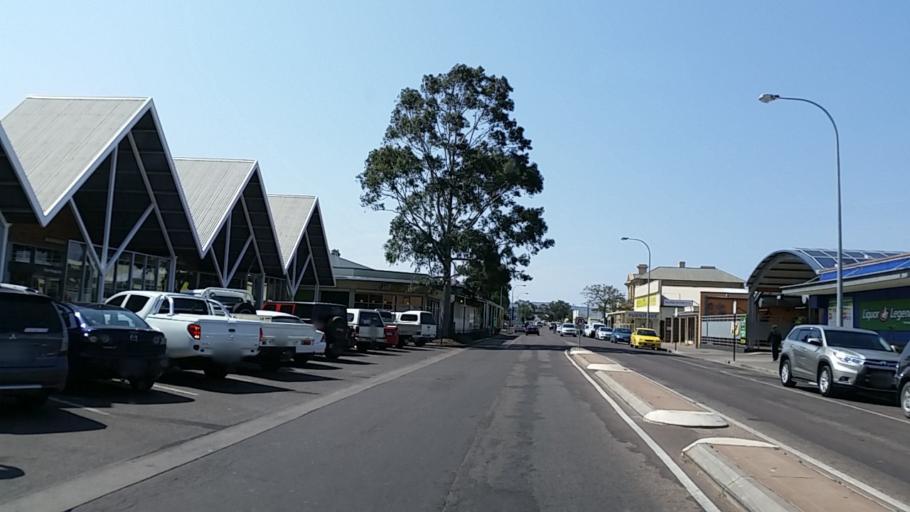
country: AU
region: South Australia
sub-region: Port Augusta
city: Port Augusta West
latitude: -32.4904
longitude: 137.7614
